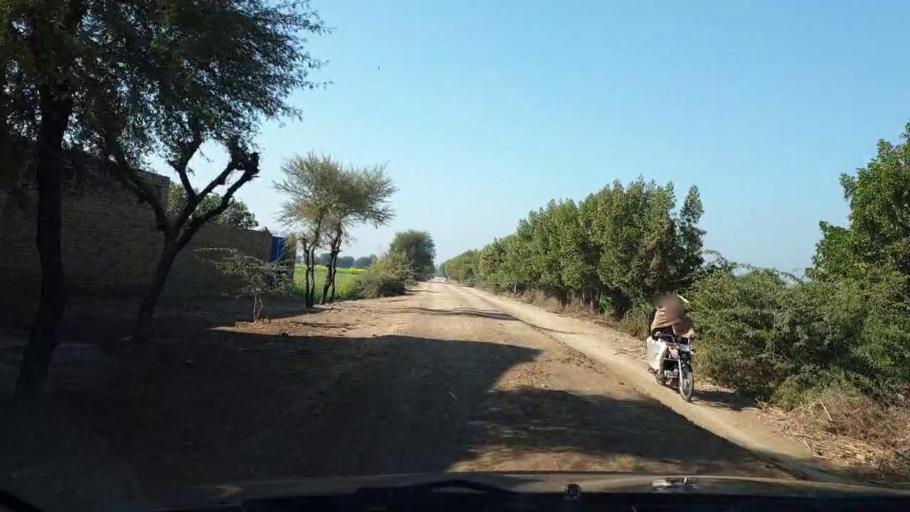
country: PK
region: Sindh
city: Sinjhoro
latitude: 25.9995
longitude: 68.7645
